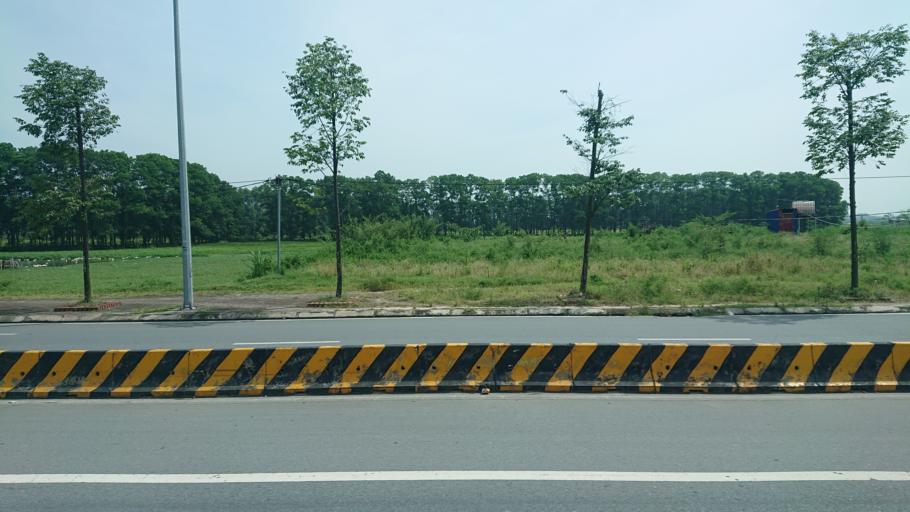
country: VN
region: Ha Noi
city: Soc Son
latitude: 21.2074
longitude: 105.8231
